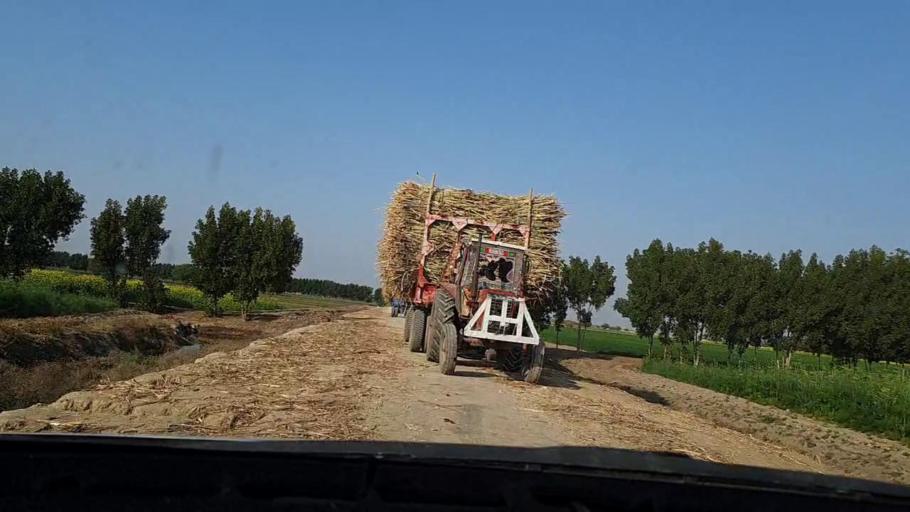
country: PK
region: Sindh
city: Tando Mittha Khan
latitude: 25.8249
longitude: 69.3064
